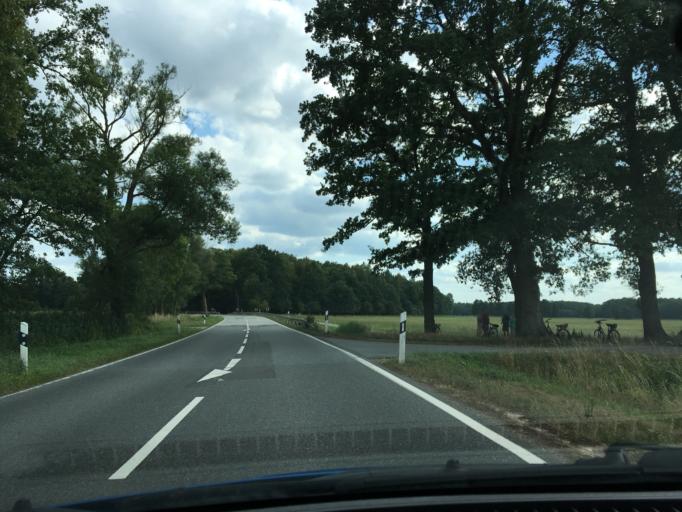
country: DE
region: Mecklenburg-Vorpommern
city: Lubtheen
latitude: 53.3620
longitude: 11.0839
